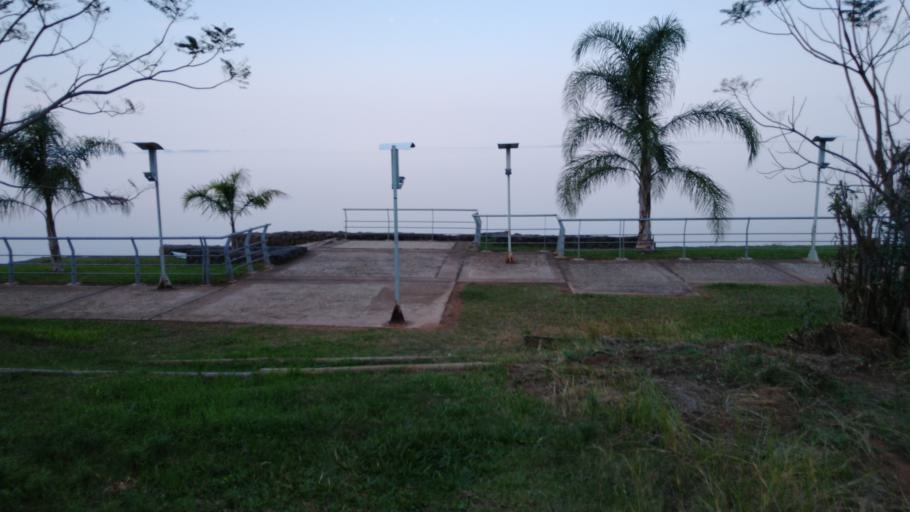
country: AR
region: Entre Rios
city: Santa Ana
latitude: -30.9109
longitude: -57.9243
